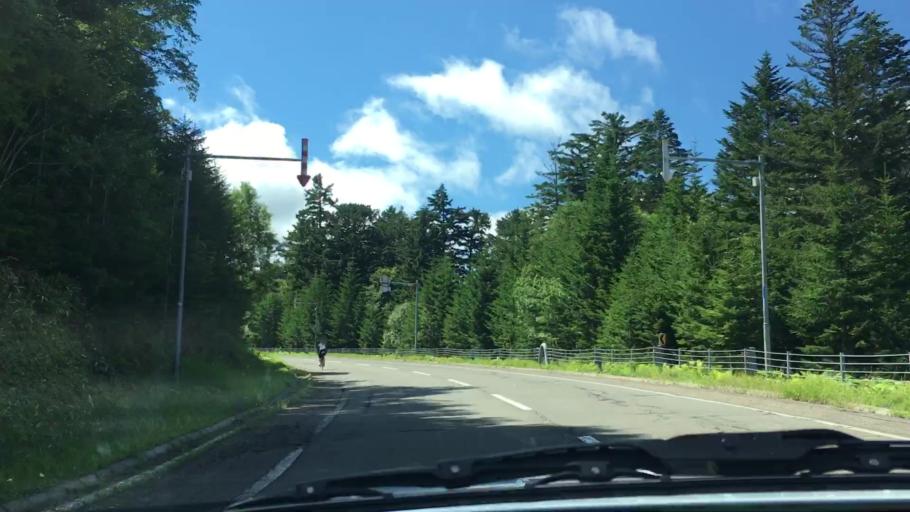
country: JP
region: Hokkaido
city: Kitami
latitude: 43.4430
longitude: 144.0132
